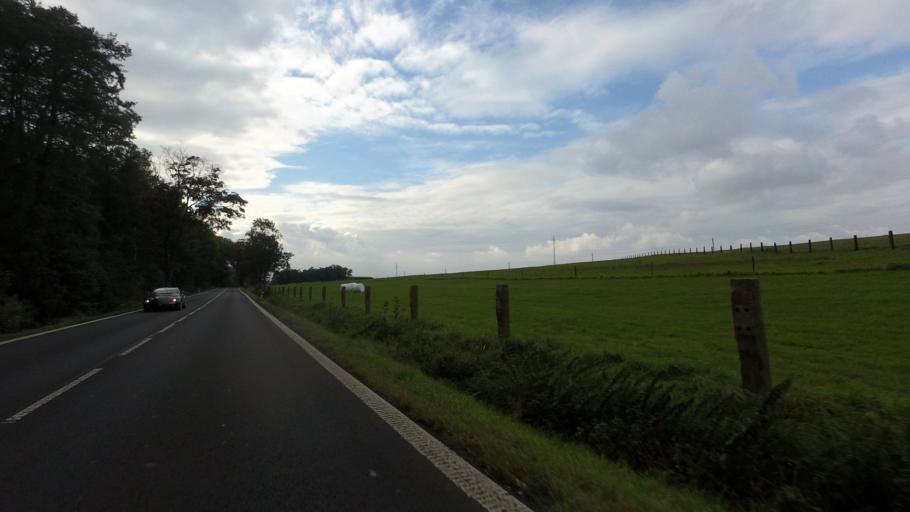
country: CZ
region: Ustecky
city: Stare Krecany
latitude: 50.9888
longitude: 14.4926
